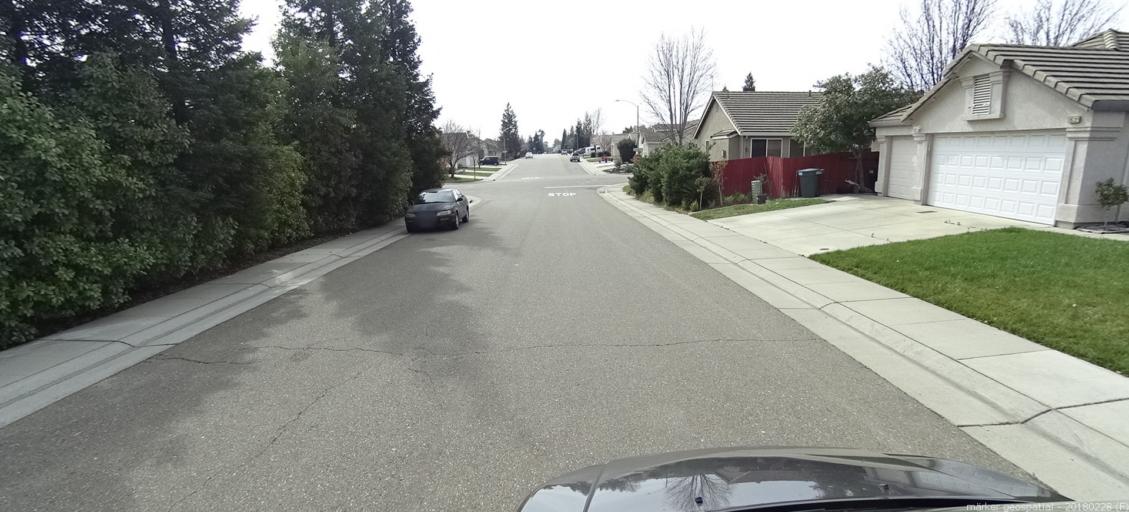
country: US
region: California
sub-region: Sacramento County
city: Antelope
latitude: 38.7226
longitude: -121.3323
